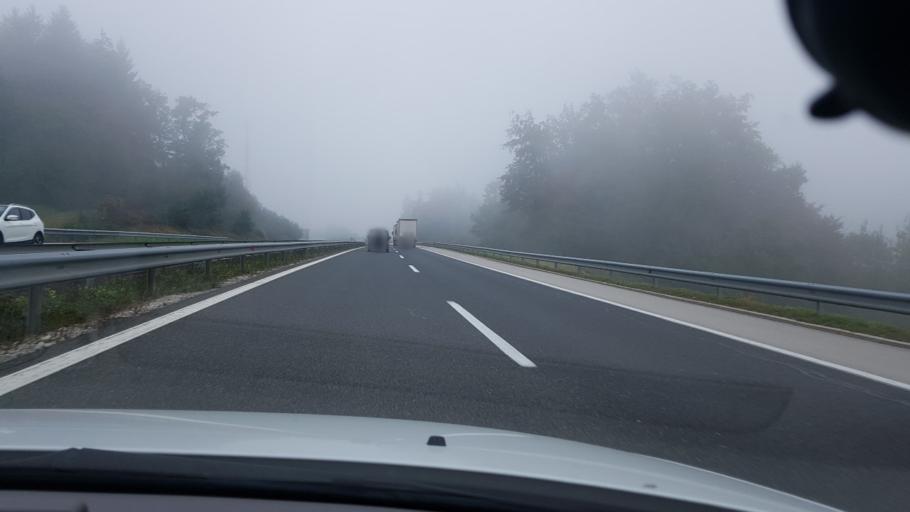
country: SI
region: Trebnje
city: Trebnje
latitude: 45.9152
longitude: 14.9559
